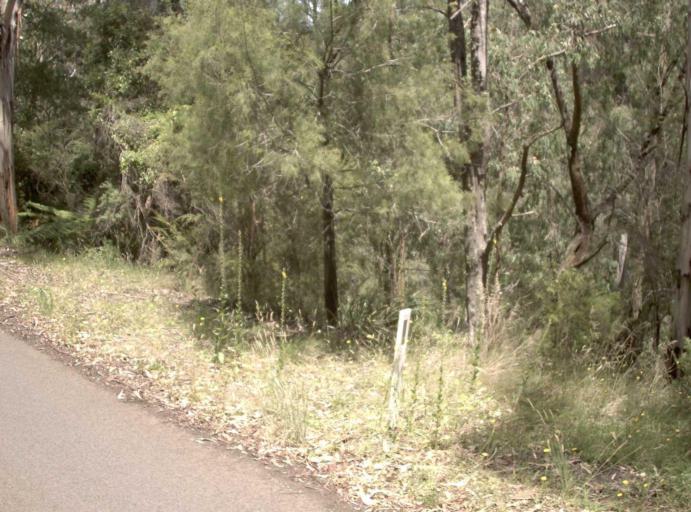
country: AU
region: Victoria
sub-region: Latrobe
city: Traralgon
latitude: -37.9692
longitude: 146.4171
